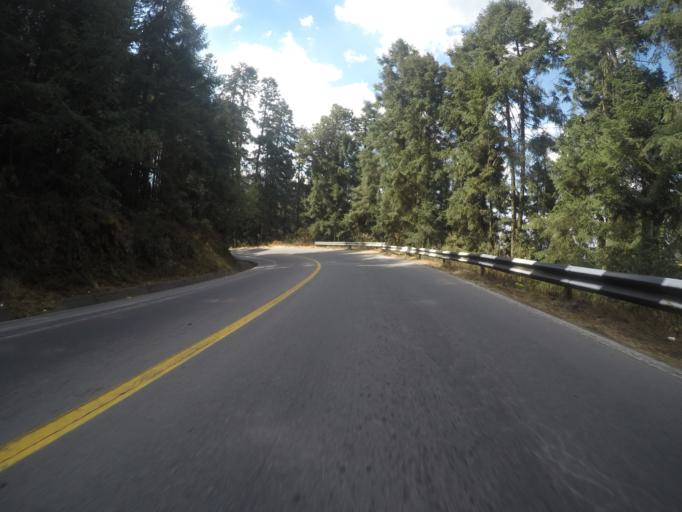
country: MX
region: Mexico
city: Cerro La Calera
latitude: 19.1755
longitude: -99.8017
